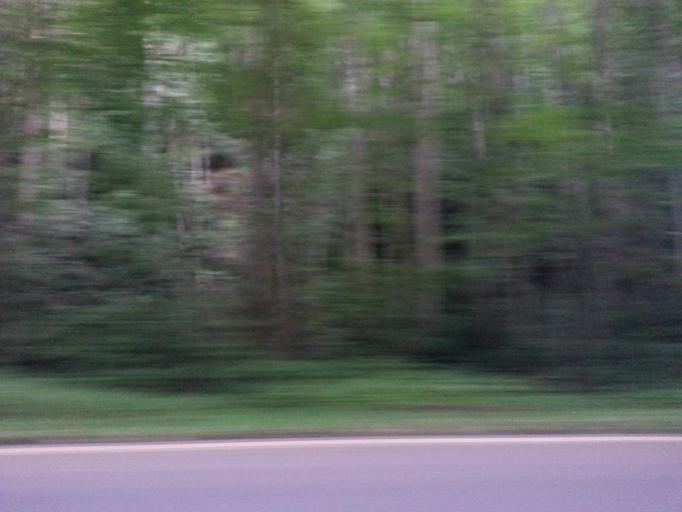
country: US
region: Tennessee
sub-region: Johnson County
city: Mountain City
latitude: 36.4682
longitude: -81.9851
